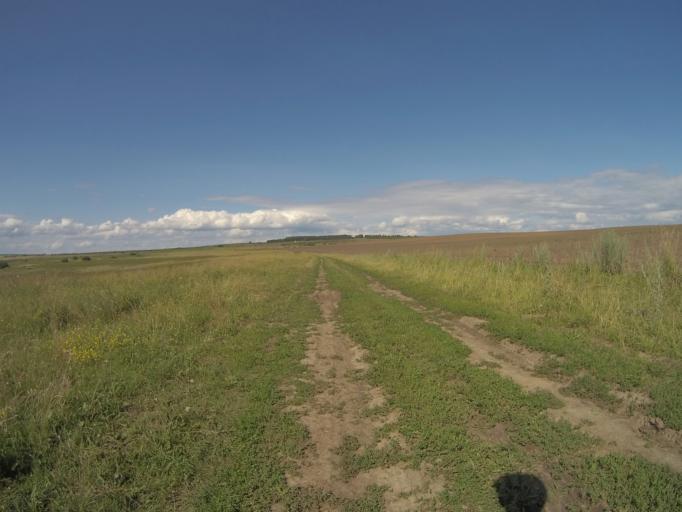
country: RU
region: Vladimir
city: Vladimir
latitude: 56.2794
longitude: 40.3465
